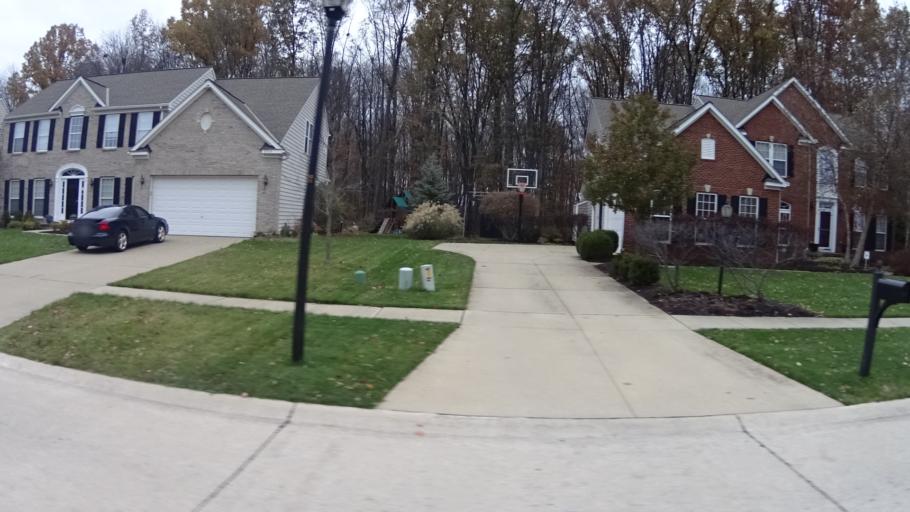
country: US
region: Ohio
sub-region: Cuyahoga County
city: Bay Village
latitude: 41.4837
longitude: -81.9725
